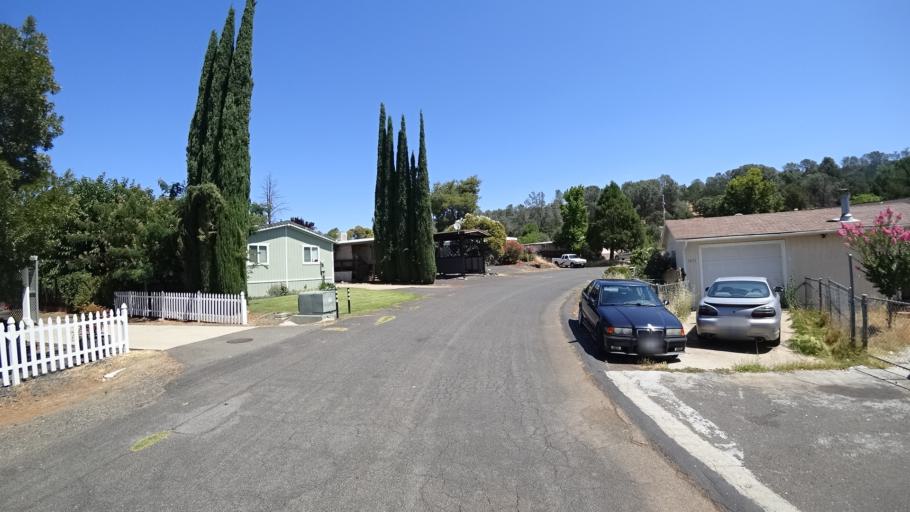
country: US
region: California
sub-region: Calaveras County
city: Copperopolis
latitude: 37.9414
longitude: -120.6076
